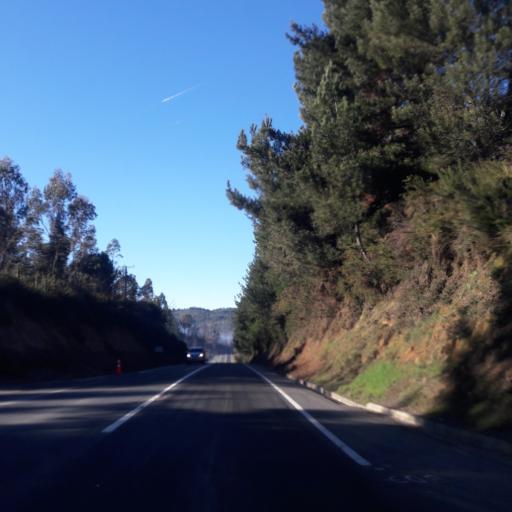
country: CL
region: Biobio
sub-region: Provincia de Biobio
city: La Laja
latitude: -37.2833
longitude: -72.9421
